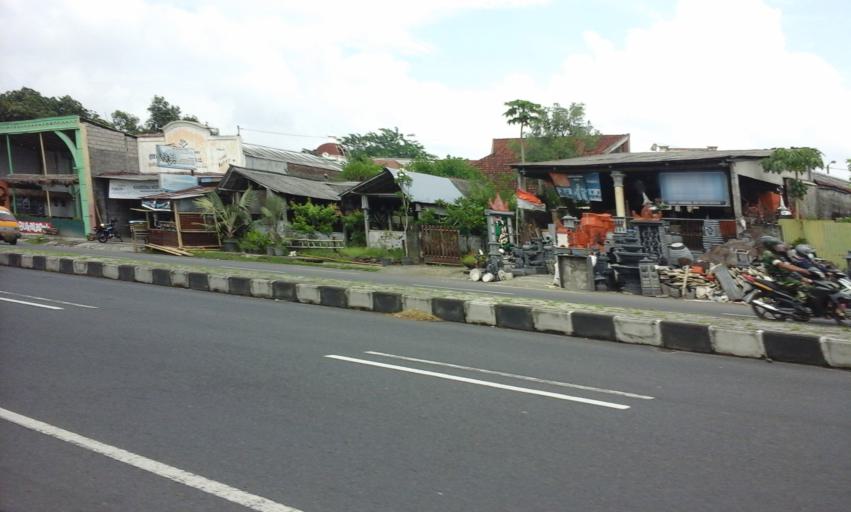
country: ID
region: East Java
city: Krajan
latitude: -8.1848
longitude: 113.6657
